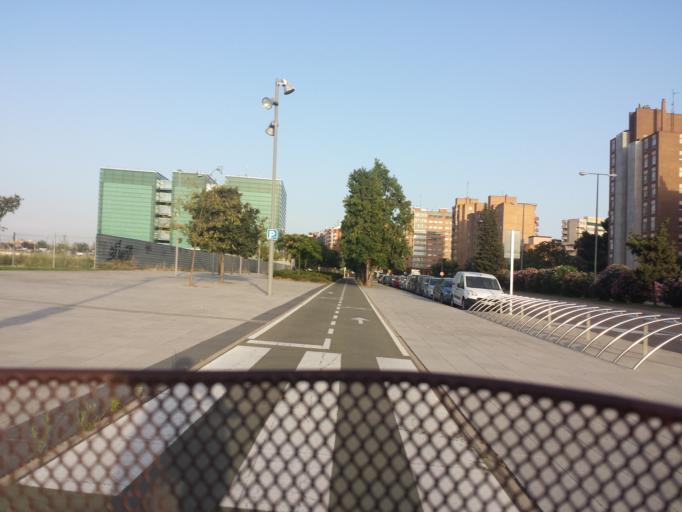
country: ES
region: Aragon
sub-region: Provincia de Zaragoza
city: Delicias
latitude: 41.6568
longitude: -0.9120
